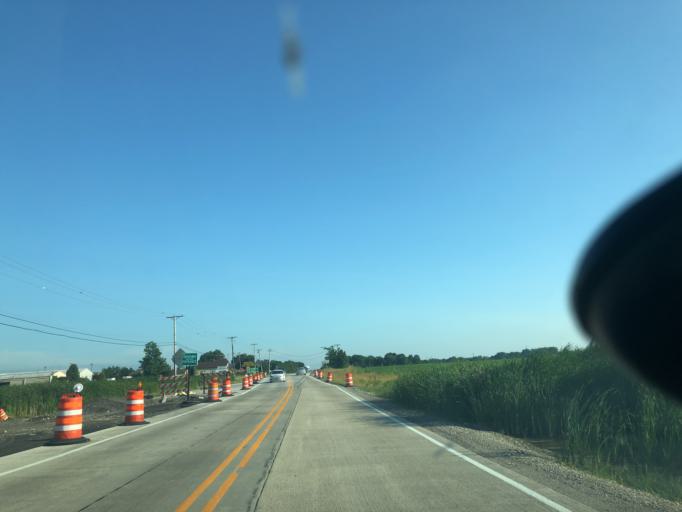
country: US
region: Illinois
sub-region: Will County
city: Homer Glen
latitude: 41.5972
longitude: -87.8914
